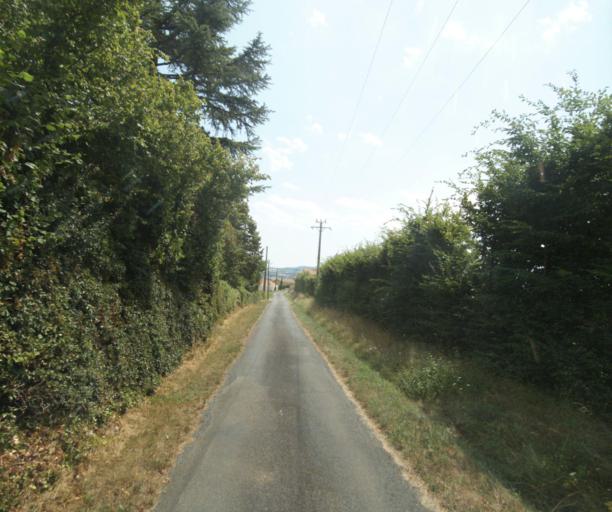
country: FR
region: Rhone-Alpes
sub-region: Departement du Rhone
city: Saint-Germain-Nuelles
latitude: 45.8627
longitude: 4.6088
